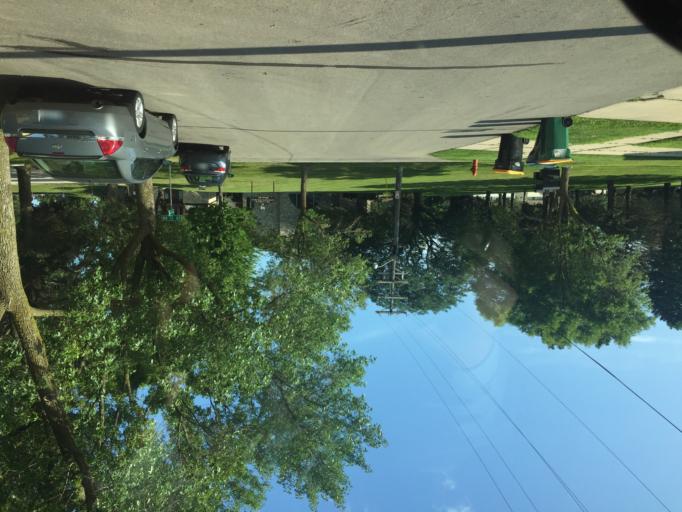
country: US
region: Minnesota
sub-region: Olmsted County
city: Rochester
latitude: 44.0444
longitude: -92.4929
